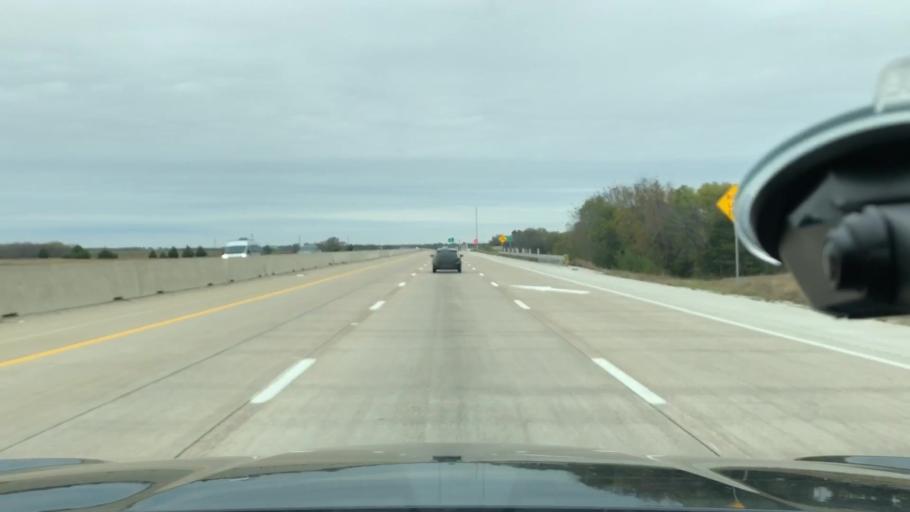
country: US
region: Texas
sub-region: Ellis County
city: Waxahachie
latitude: 32.3342
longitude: -96.8575
